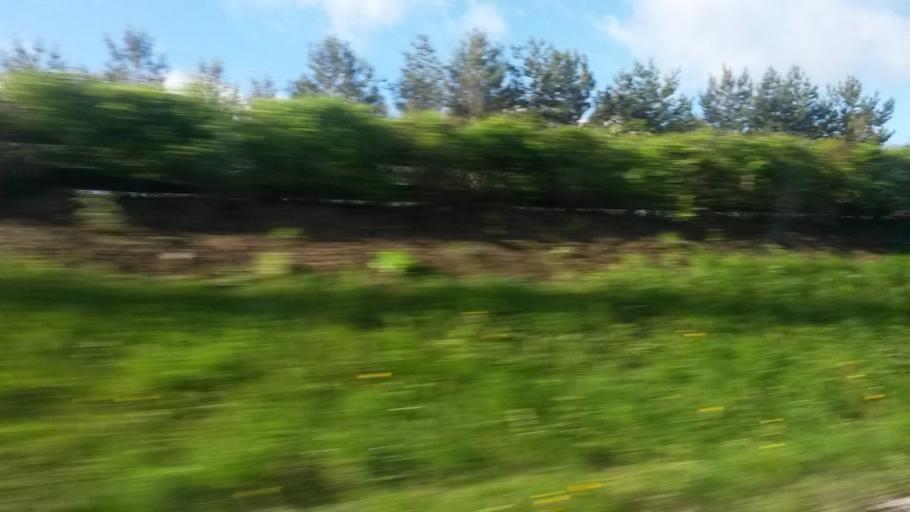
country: IE
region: Munster
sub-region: County Cork
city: Passage West
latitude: 51.9063
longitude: -8.3943
